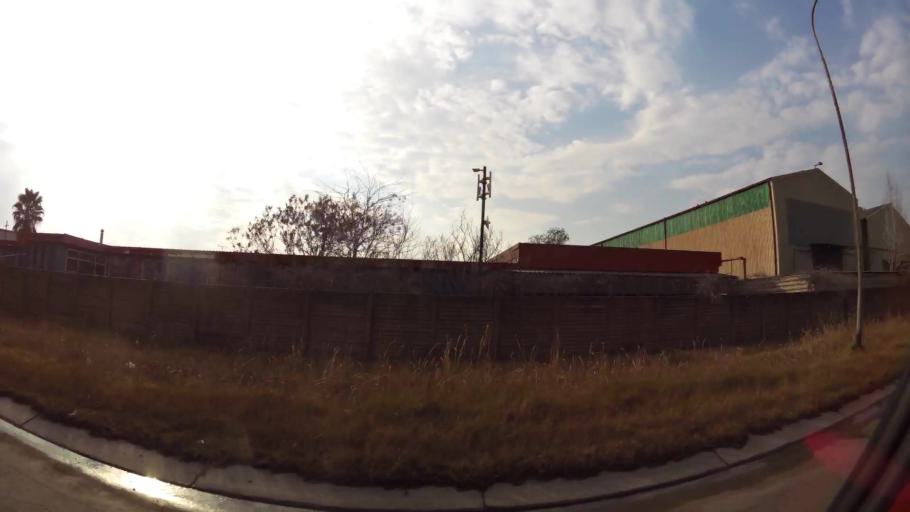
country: ZA
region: Gauteng
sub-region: Sedibeng District Municipality
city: Vereeniging
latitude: -26.6818
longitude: 27.9078
